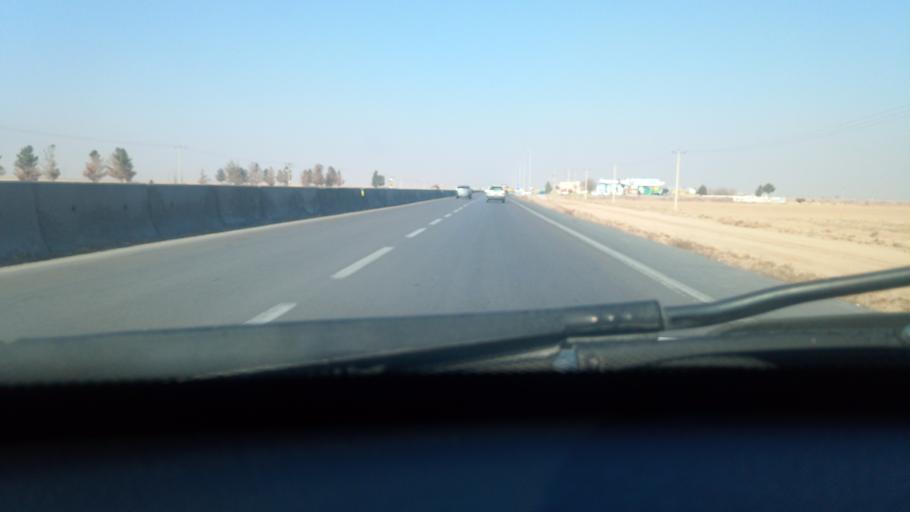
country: IR
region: Razavi Khorasan
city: Chenaran
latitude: 36.7773
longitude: 58.9029
